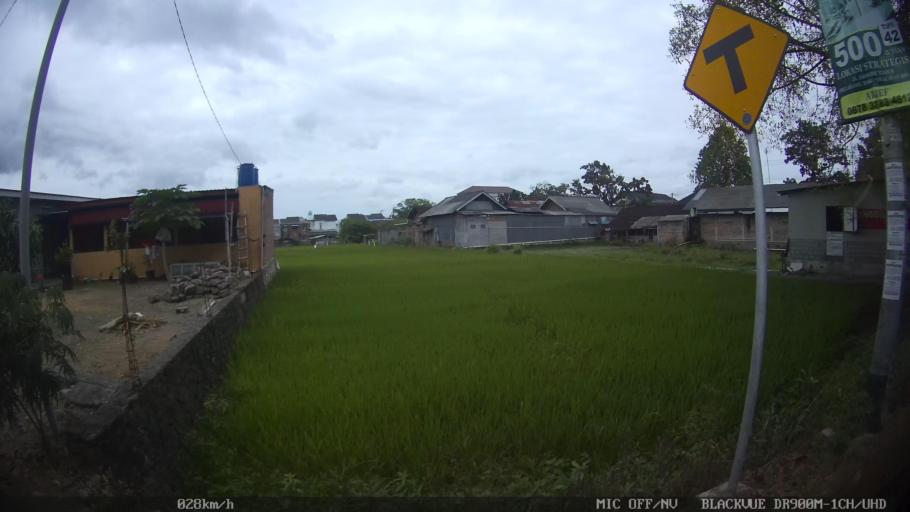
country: ID
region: Daerah Istimewa Yogyakarta
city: Sewon
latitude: -7.8492
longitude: 110.3914
